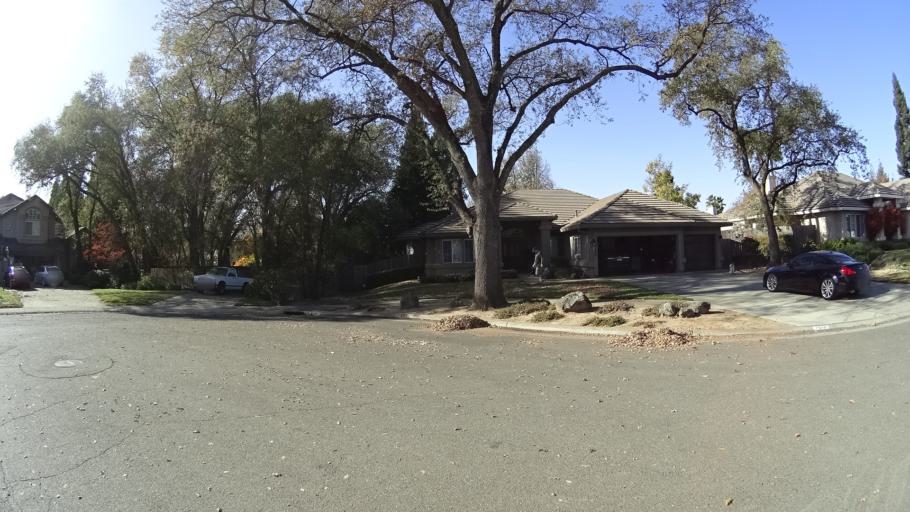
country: US
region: California
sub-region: Sacramento County
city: Citrus Heights
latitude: 38.7028
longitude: -121.2767
